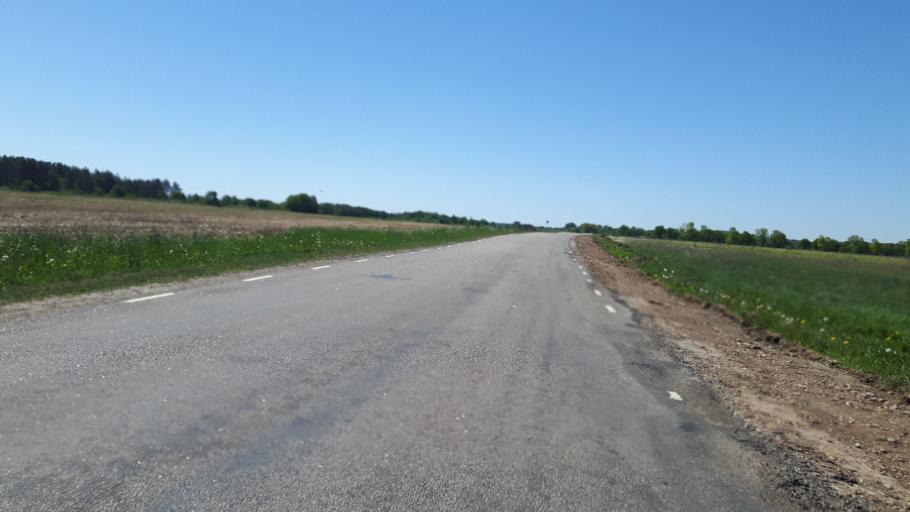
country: EE
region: Ida-Virumaa
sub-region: Narva-Joesuu linn
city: Narva-Joesuu
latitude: 59.4018
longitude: 27.9362
